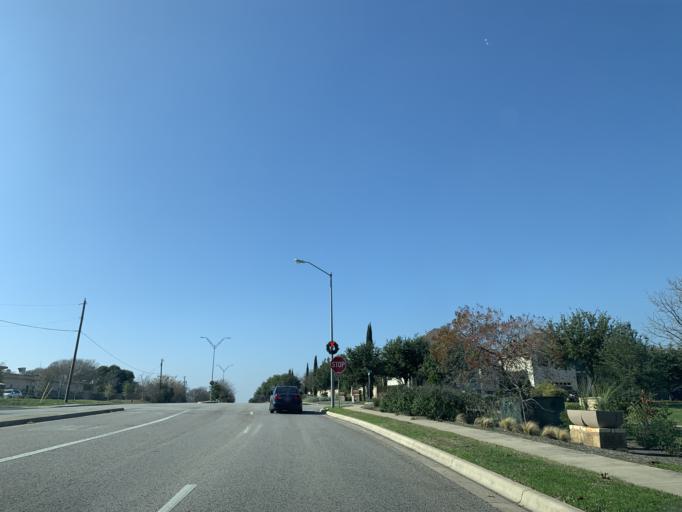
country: US
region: Texas
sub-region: Williamson County
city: Round Rock
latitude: 30.5088
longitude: -97.6295
